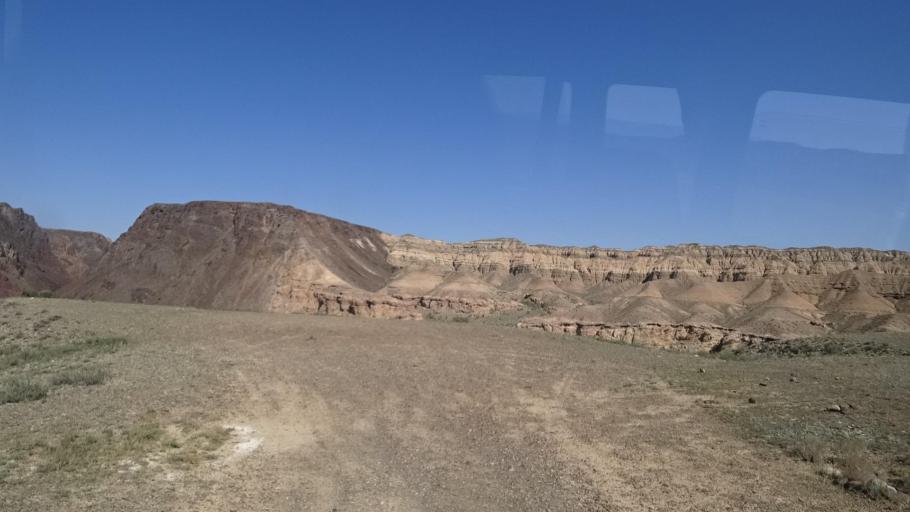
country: KZ
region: Almaty Oblysy
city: Kegen
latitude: 43.2741
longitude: 78.9752
